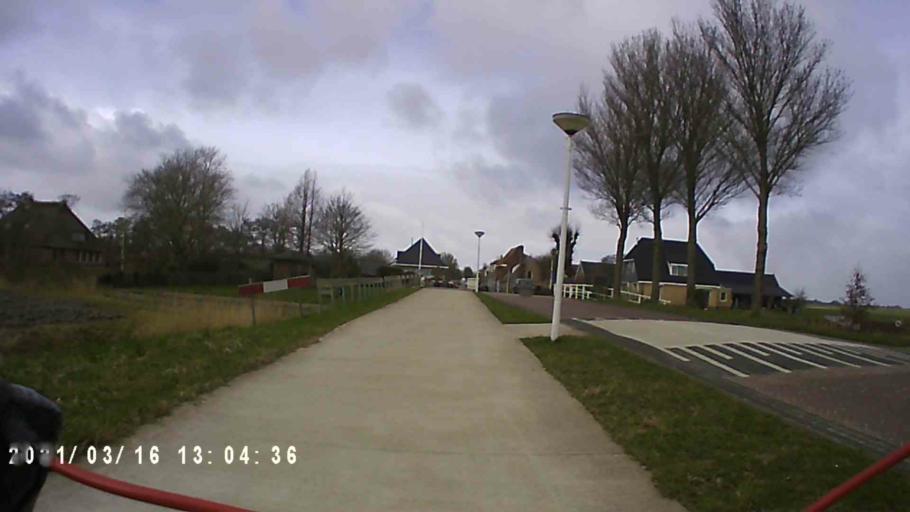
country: NL
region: Friesland
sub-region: Menameradiel
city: Berltsum
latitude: 53.2510
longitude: 5.6309
